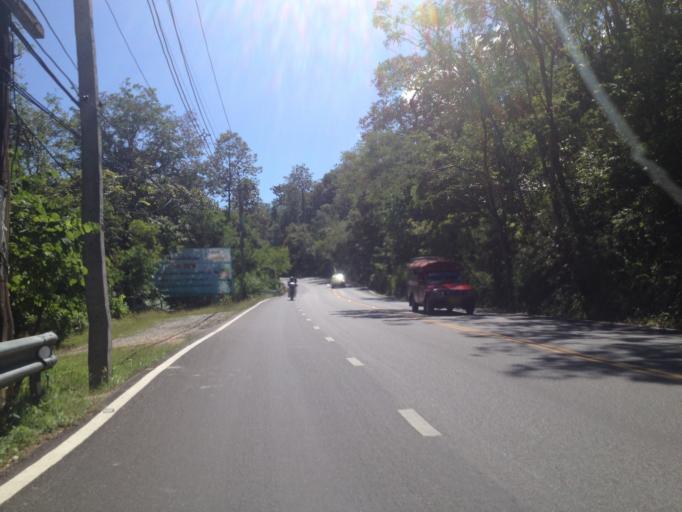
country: TH
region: Chiang Mai
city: Chiang Mai
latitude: 18.8068
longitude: 98.9376
